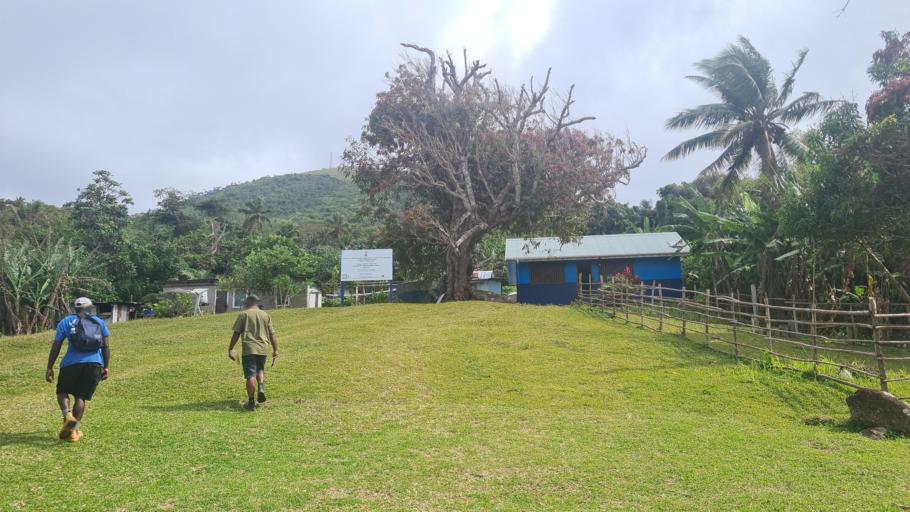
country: VU
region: Shefa
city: Port-Vila
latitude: -17.4917
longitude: 168.4893
